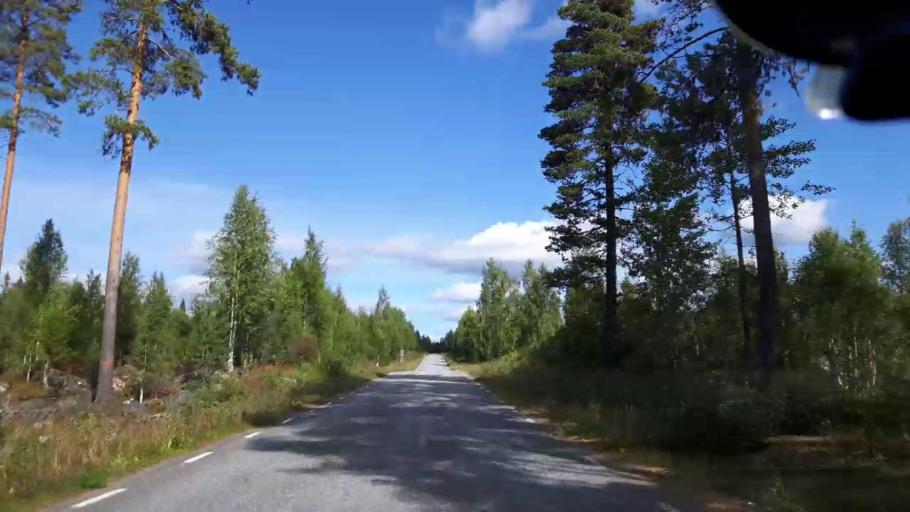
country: SE
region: Jaemtland
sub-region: OEstersunds Kommun
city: Brunflo
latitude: 63.1932
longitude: 15.2196
